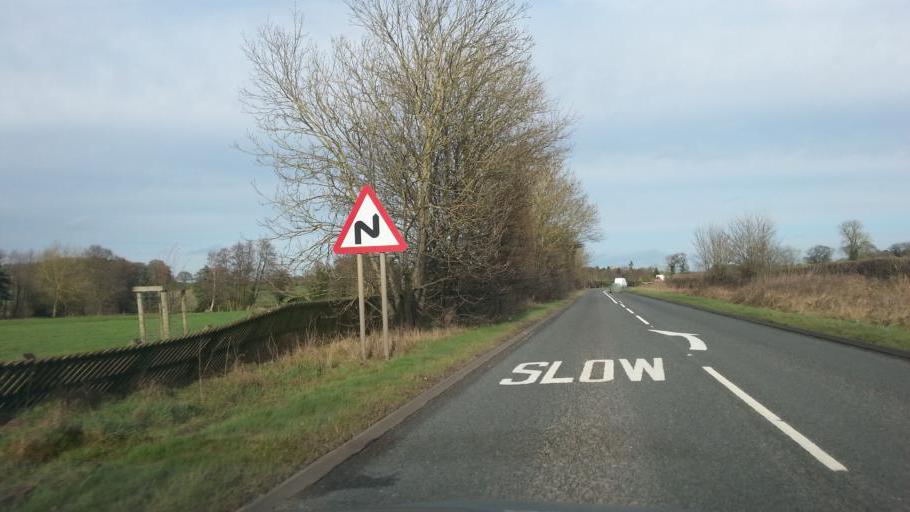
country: GB
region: England
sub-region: Staffordshire
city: Colwich
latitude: 52.8478
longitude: -2.0014
